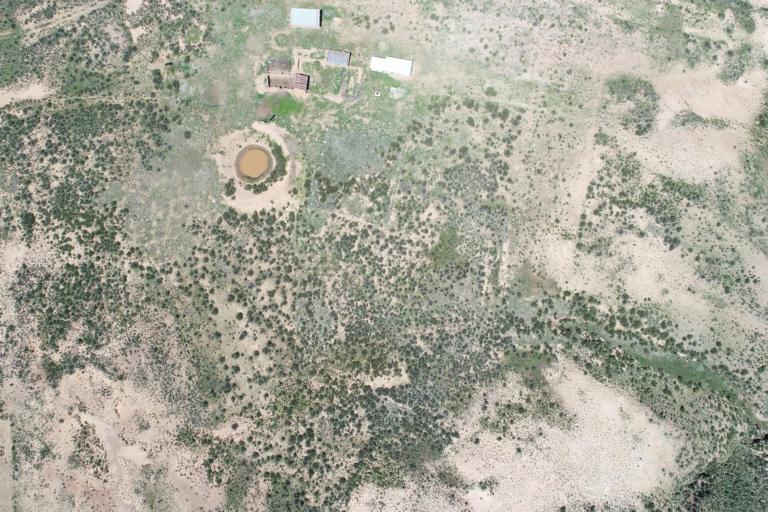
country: BO
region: La Paz
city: Curahuara de Carangas
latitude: -17.3222
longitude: -68.4982
